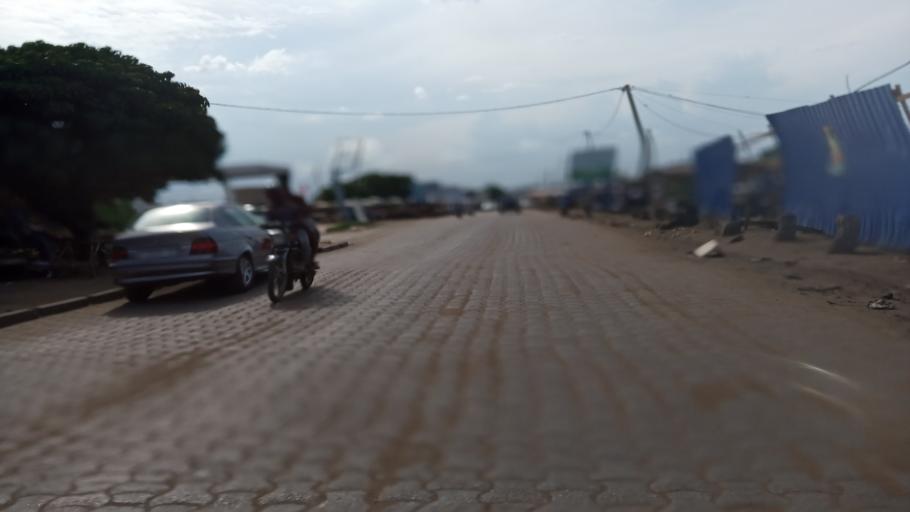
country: TG
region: Maritime
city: Lome
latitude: 6.1525
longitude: 1.2698
